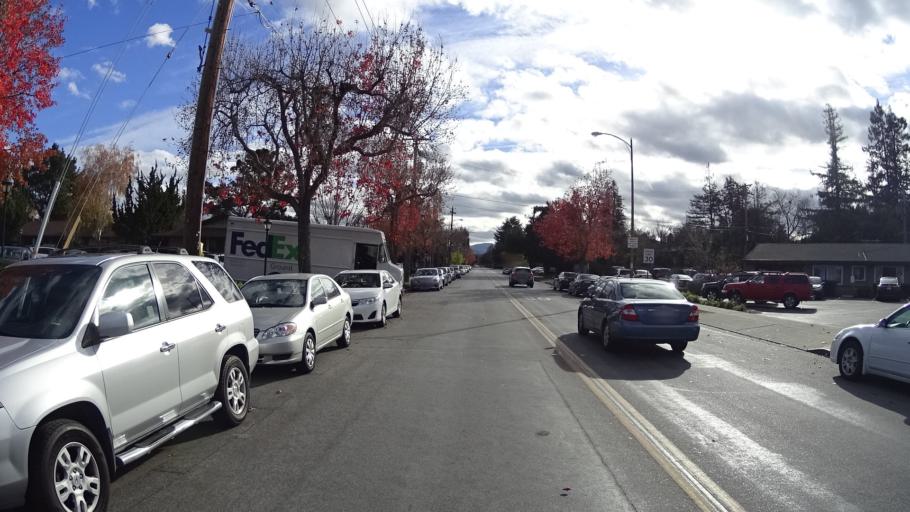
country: US
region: California
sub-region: Santa Clara County
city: Sunnyvale
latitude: 37.3517
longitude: -122.0551
